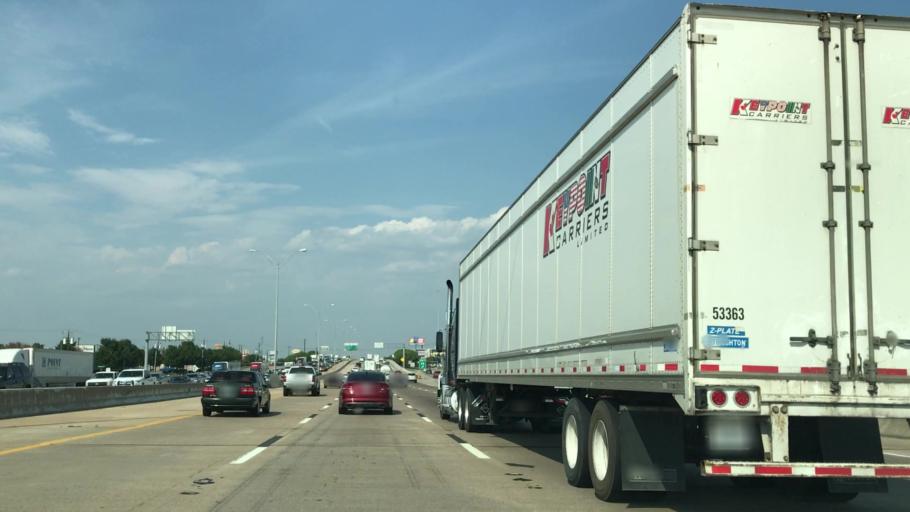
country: US
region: Texas
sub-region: Dallas County
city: Sunnyvale
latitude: 32.8374
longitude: -96.6018
